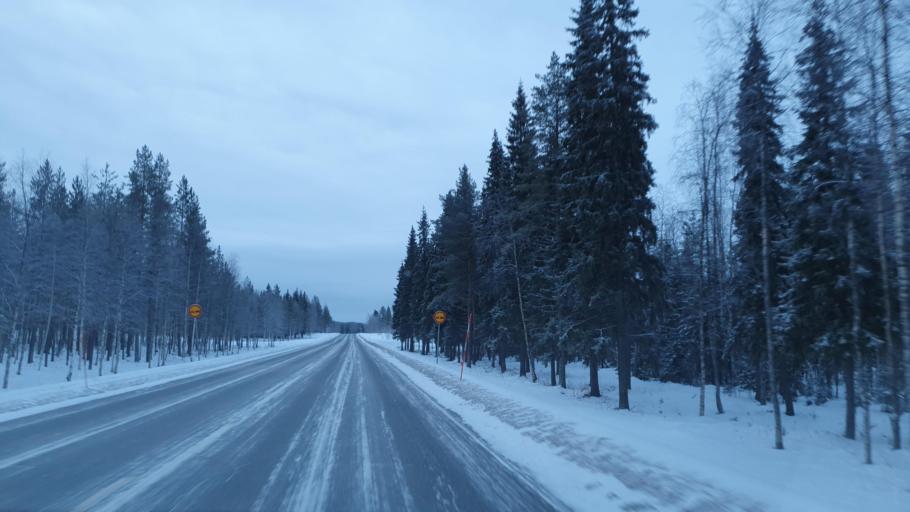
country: SE
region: Norrbotten
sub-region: Overtornea Kommun
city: OEvertornea
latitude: 66.4888
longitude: 23.7412
